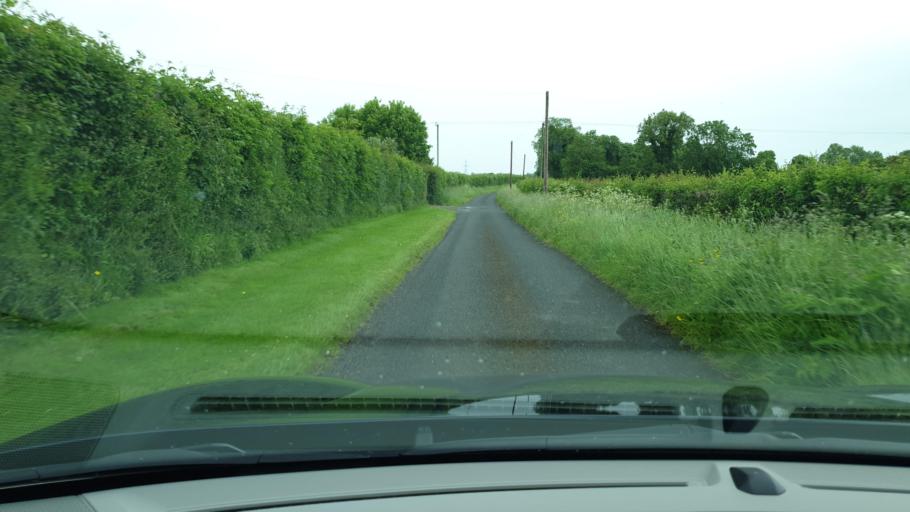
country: IE
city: Confey
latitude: 53.4289
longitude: -6.5327
